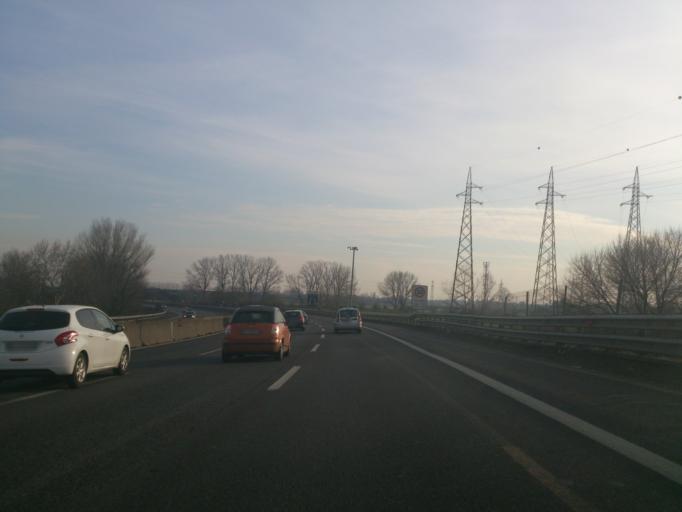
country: IT
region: Lombardy
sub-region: Citta metropolitana di Milano
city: Chiaravalle
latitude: 45.4198
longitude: 9.2461
